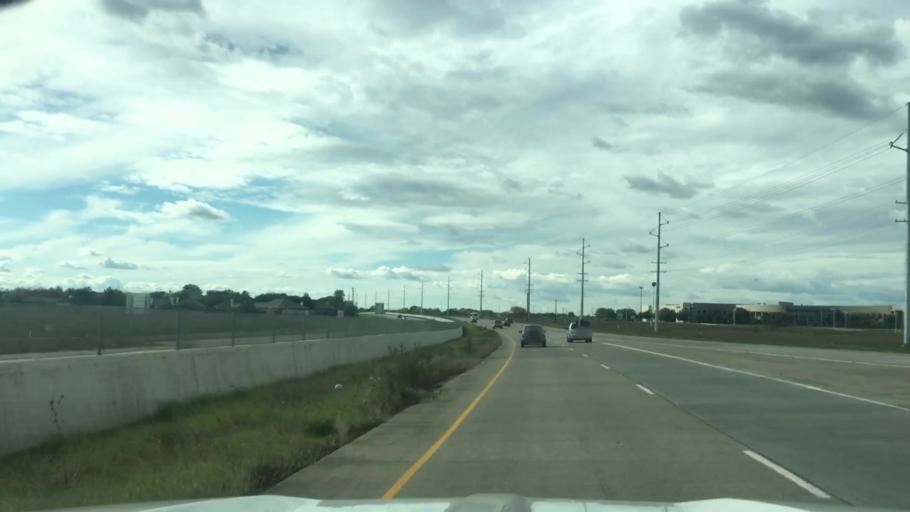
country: US
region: Texas
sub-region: Denton County
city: Denton
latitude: 33.2594
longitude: -97.1131
